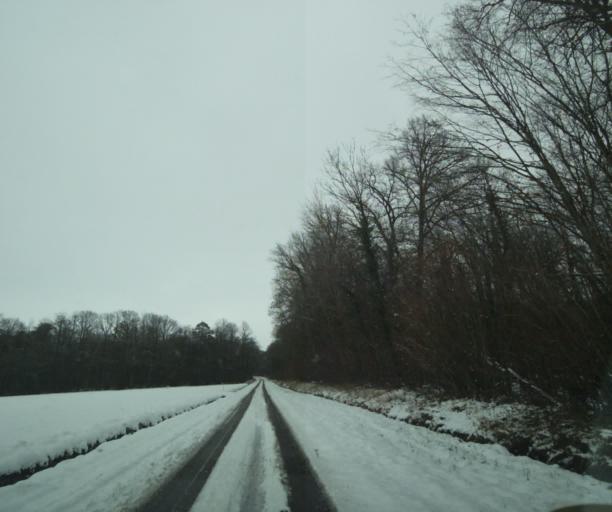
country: FR
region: Champagne-Ardenne
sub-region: Departement de la Haute-Marne
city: Montier-en-Der
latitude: 48.4175
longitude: 4.7583
